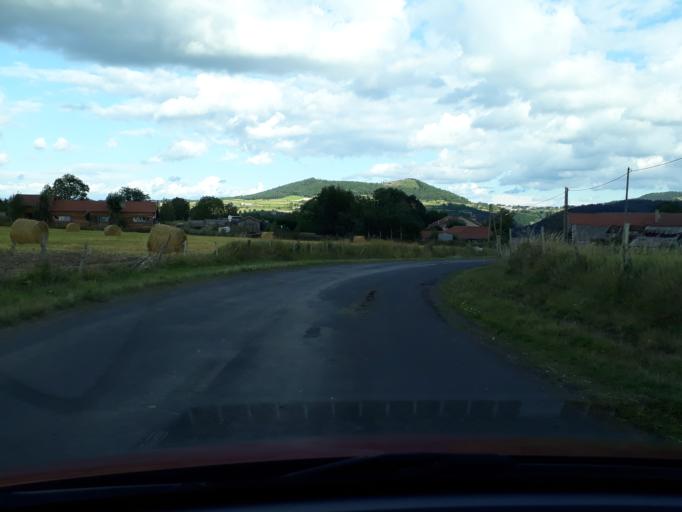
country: FR
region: Languedoc-Roussillon
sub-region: Departement de la Lozere
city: Langogne
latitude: 44.8220
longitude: 3.9271
